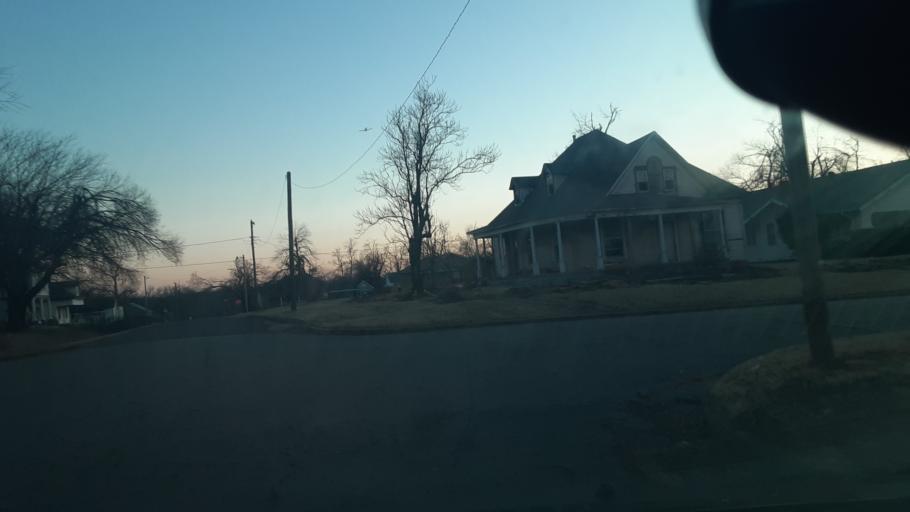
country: US
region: Oklahoma
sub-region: Logan County
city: Guthrie
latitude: 35.8750
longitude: -97.4202
